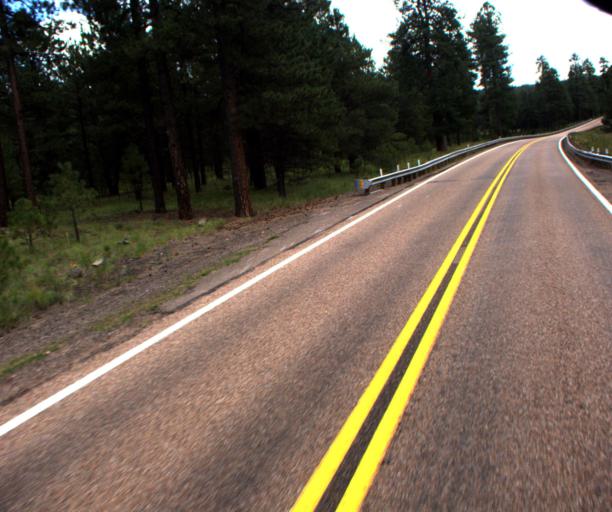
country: US
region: Arizona
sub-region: Navajo County
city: Pinetop-Lakeside
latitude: 34.0372
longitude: -109.6667
